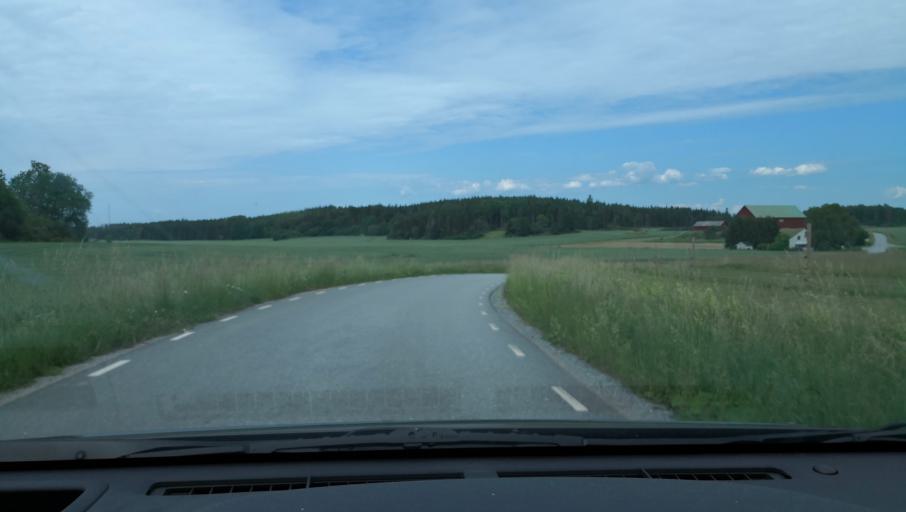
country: SE
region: Uppsala
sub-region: Habo Kommun
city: Balsta
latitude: 59.7019
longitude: 17.4751
